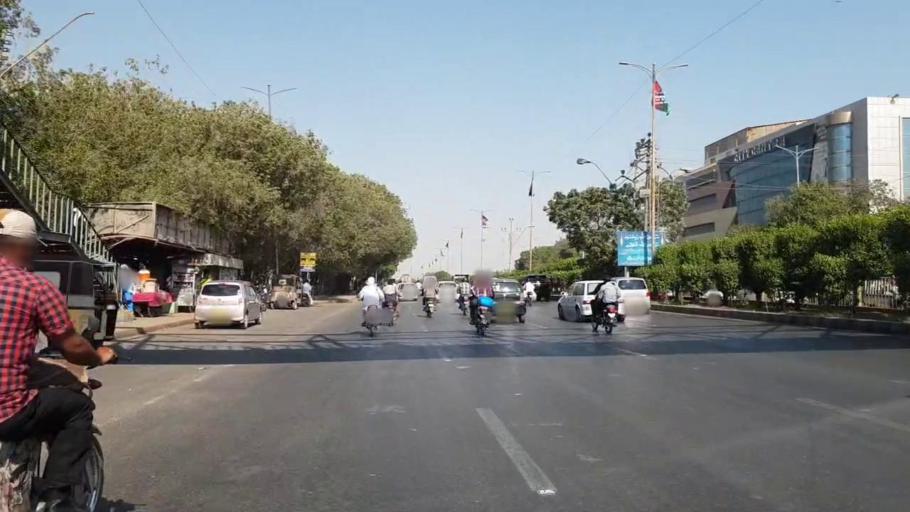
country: PK
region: Sindh
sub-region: Karachi District
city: Karachi
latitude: 24.8711
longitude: 67.0895
